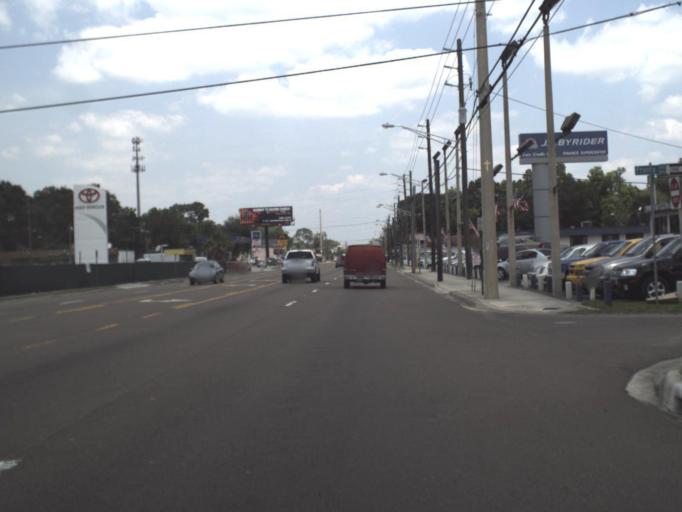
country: US
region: Florida
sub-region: Duval County
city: Jacksonville
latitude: 30.2993
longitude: -81.7304
